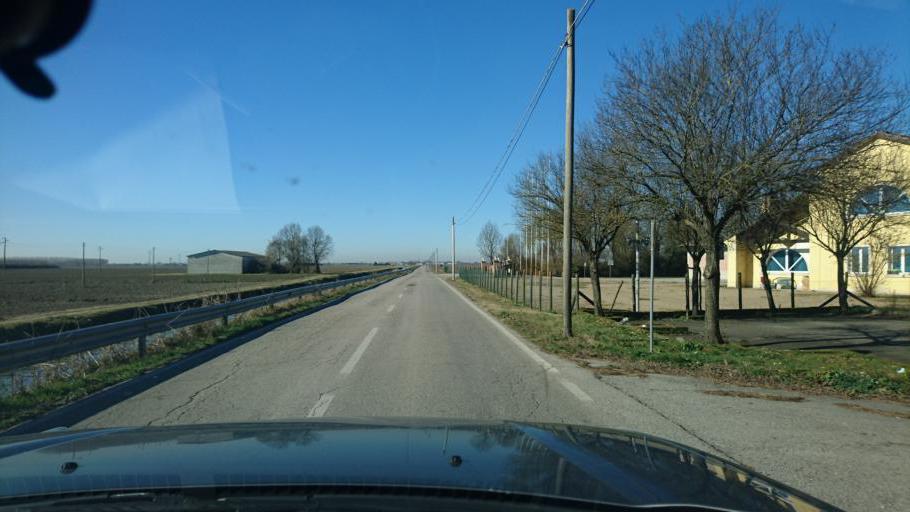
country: IT
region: Emilia-Romagna
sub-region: Provincia di Ferrara
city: Mesola
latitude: 44.9469
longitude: 12.2599
